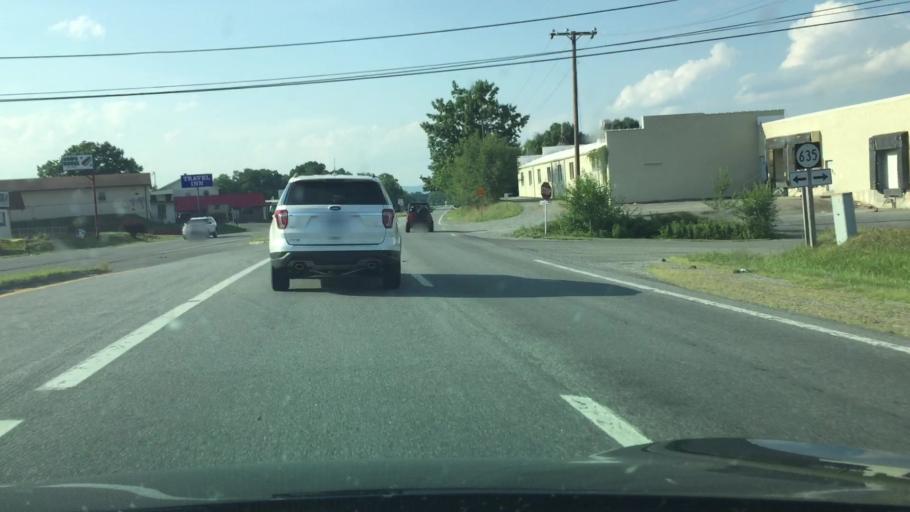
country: US
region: Virginia
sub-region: Pulaski County
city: Dublin
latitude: 37.0974
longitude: -80.6905
